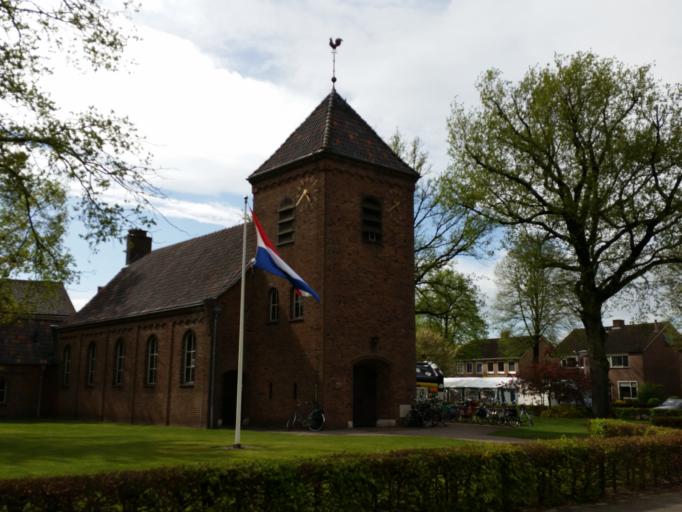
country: NL
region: Overijssel
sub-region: Gemeente Dalfsen
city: Dalfsen
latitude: 52.5323
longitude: 6.3118
